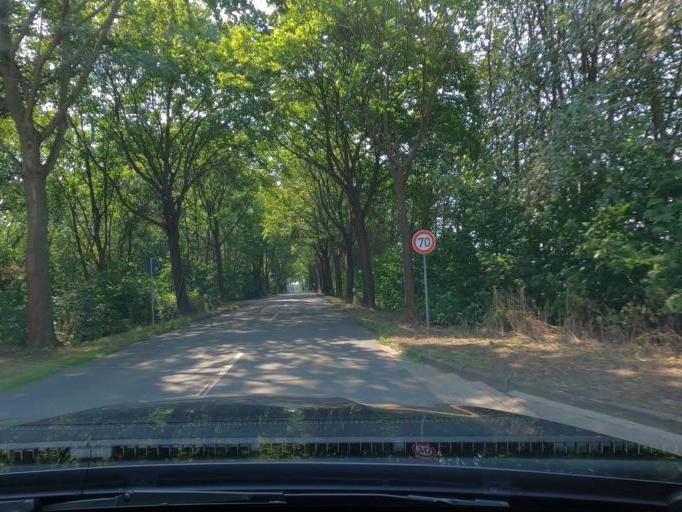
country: DE
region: Lower Saxony
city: Sarstedt
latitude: 52.2437
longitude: 9.8243
